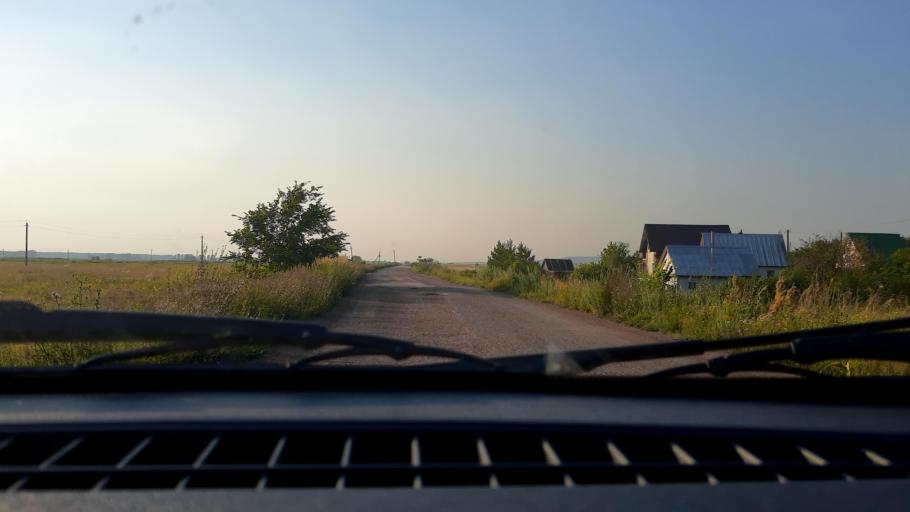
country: RU
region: Bashkortostan
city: Asanovo
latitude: 54.9164
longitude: 55.6270
